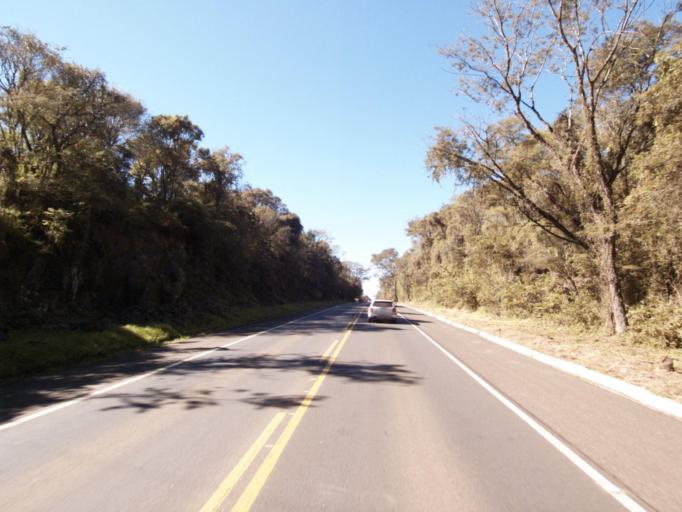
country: BR
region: Santa Catarina
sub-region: Chapeco
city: Chapeco
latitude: -26.8992
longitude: -52.8820
